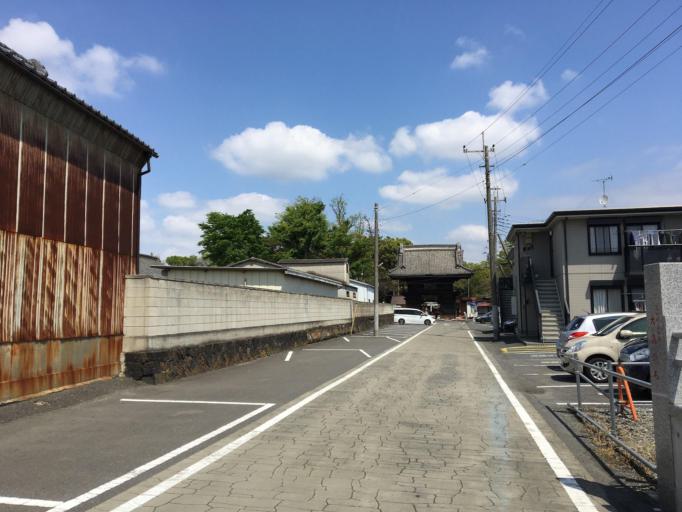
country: JP
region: Gunma
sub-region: Sawa-gun
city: Tamamura
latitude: 36.3033
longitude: 139.1084
